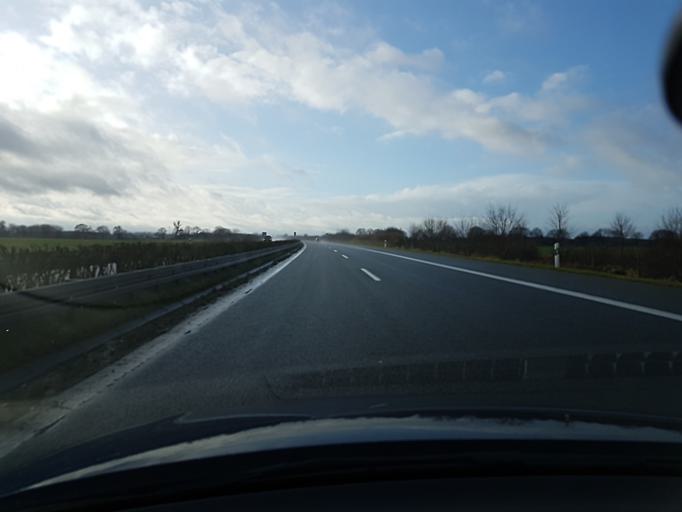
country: DE
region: Mecklenburg-Vorpommern
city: Bad Sulze
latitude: 54.0503
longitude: 12.6214
